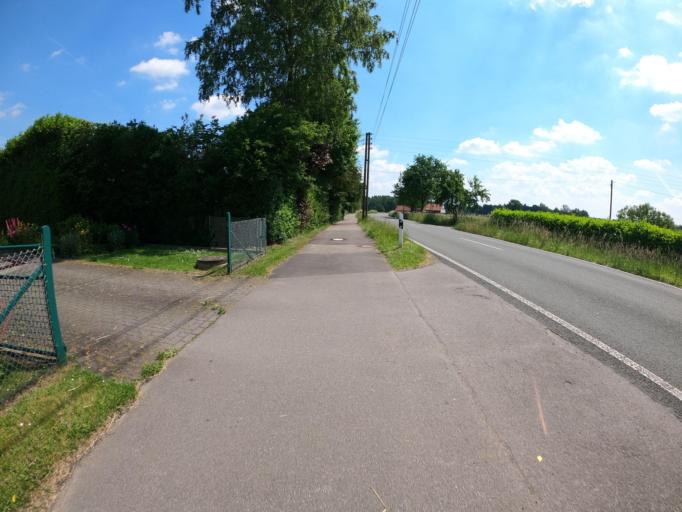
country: DE
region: North Rhine-Westphalia
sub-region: Regierungsbezirk Dusseldorf
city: Hunxe
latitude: 51.7142
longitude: 6.7694
